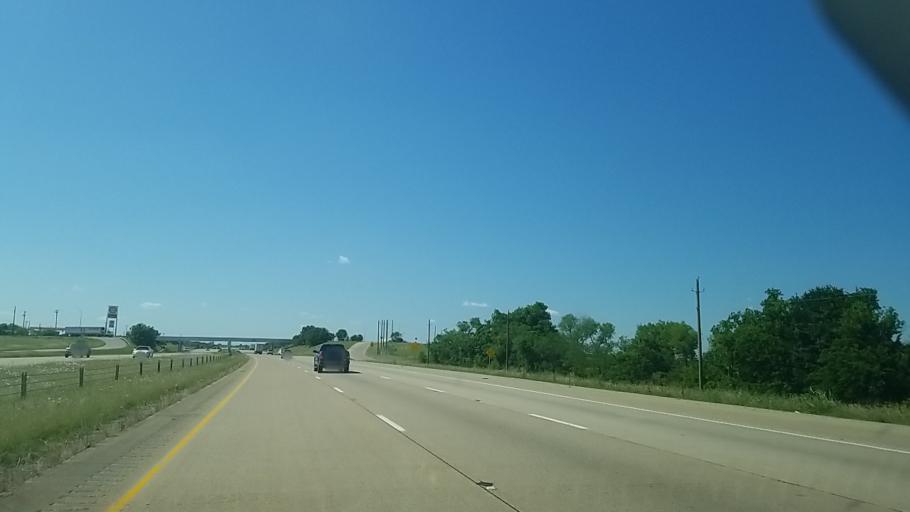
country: US
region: Texas
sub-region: Ellis County
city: Ennis
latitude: 32.3567
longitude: -96.6296
